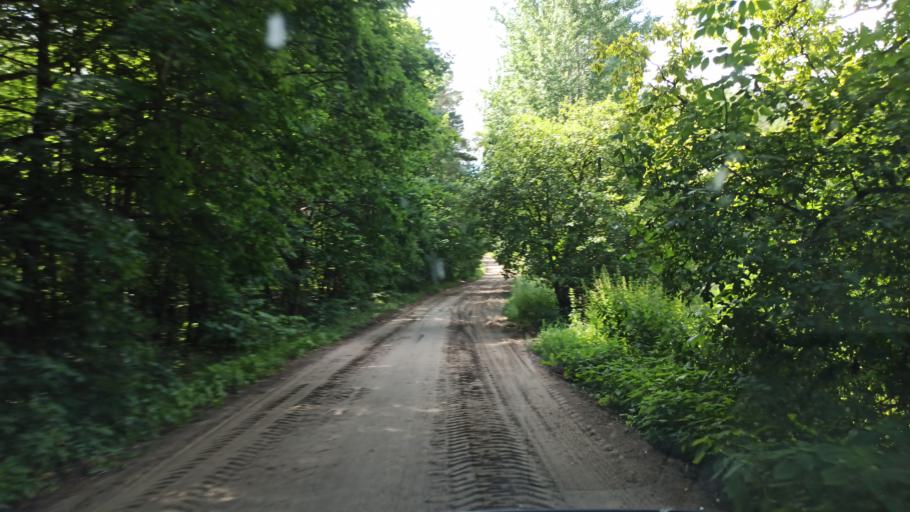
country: PL
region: Warmian-Masurian Voivodeship
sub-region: Powiat ostrodzki
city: Morag
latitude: 53.8669
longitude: 20.0465
